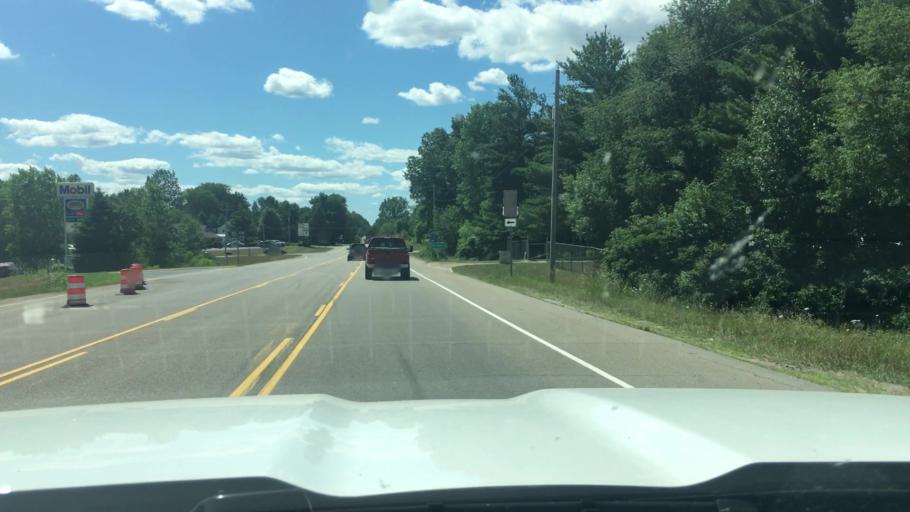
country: US
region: Michigan
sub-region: Kent County
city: Cedar Springs
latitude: 43.1756
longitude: -85.5788
